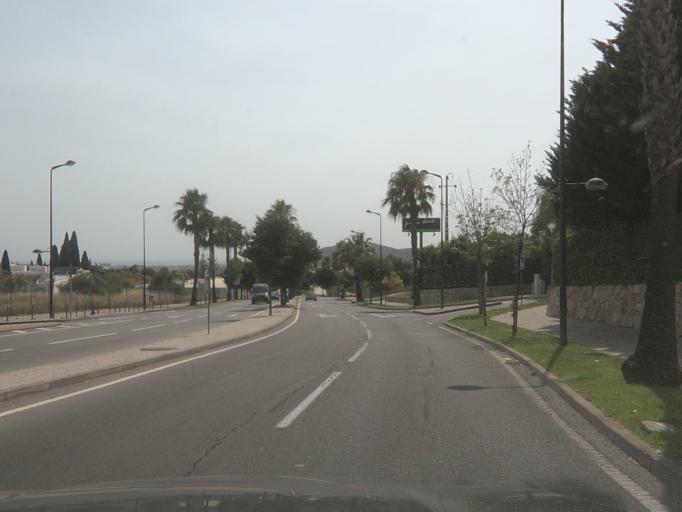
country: PT
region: Faro
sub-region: Loule
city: Loule
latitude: 37.1376
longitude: -8.0290
